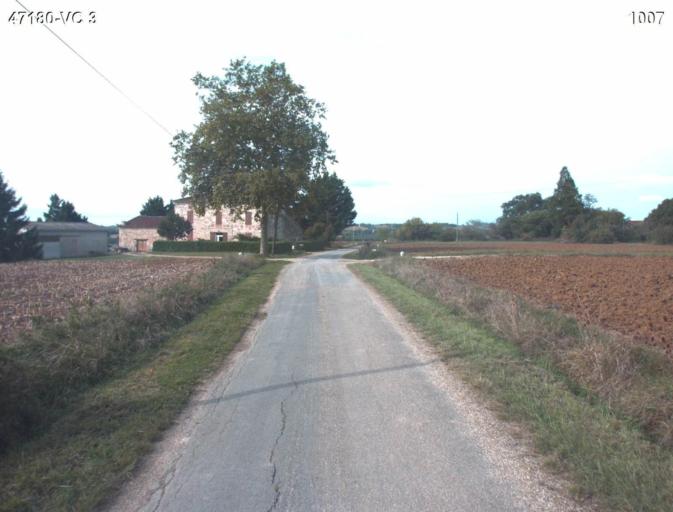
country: FR
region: Aquitaine
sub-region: Departement du Lot-et-Garonne
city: Sainte-Colombe-en-Bruilhois
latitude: 44.1595
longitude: 0.4445
